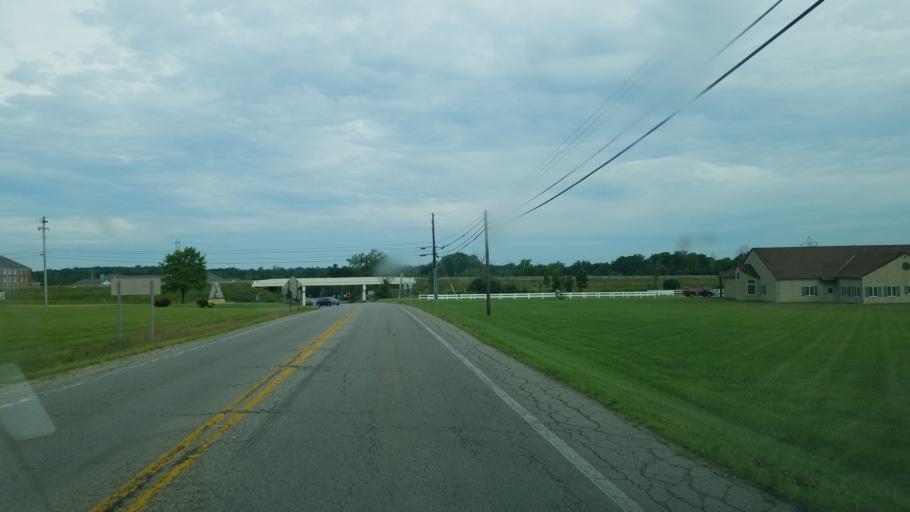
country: US
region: Ohio
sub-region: Ashland County
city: Ashland
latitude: 40.8452
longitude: -82.2958
